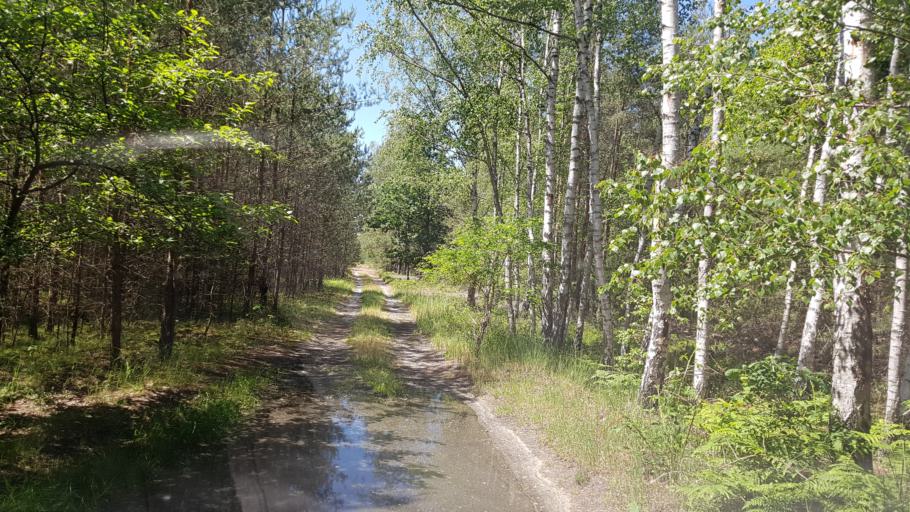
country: DE
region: Brandenburg
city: Ruckersdorf
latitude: 51.5462
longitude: 13.5540
